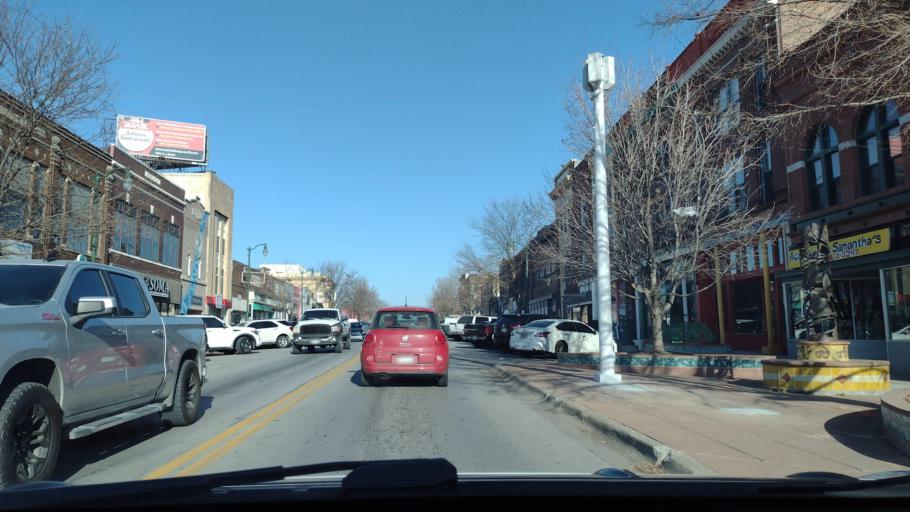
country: US
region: Nebraska
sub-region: Douglas County
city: Omaha
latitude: 41.2098
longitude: -95.9471
